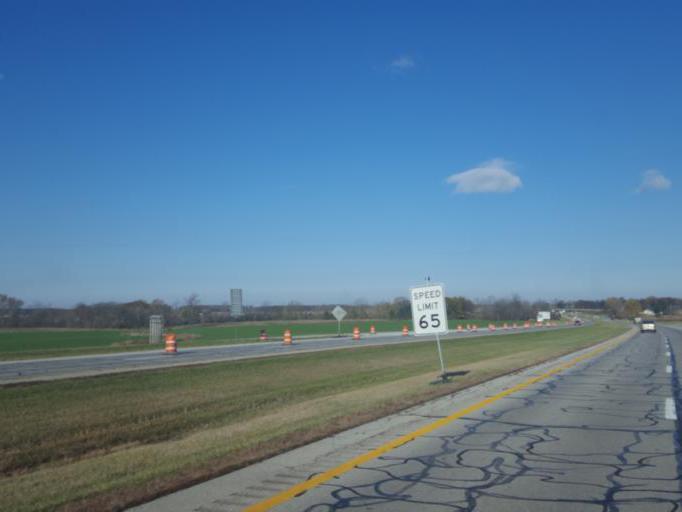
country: US
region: Ohio
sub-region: Marion County
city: Marion
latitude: 40.6657
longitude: -83.1113
